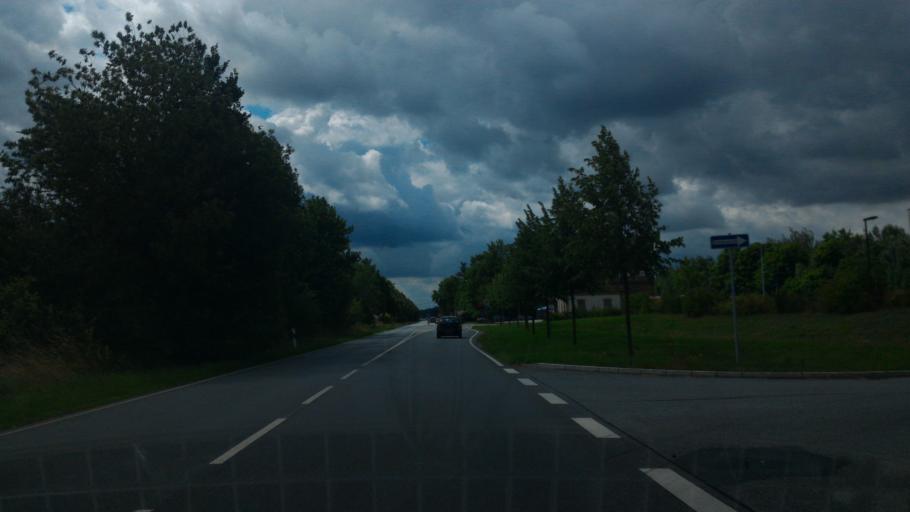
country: DE
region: Saxony
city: Ostritz
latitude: 51.0714
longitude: 14.9615
